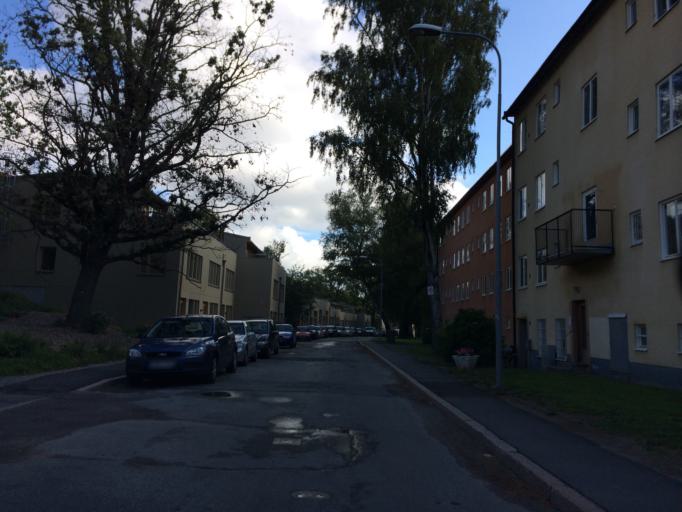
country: SE
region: Stockholm
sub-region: Stockholms Kommun
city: Arsta
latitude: 59.3021
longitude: 17.9973
